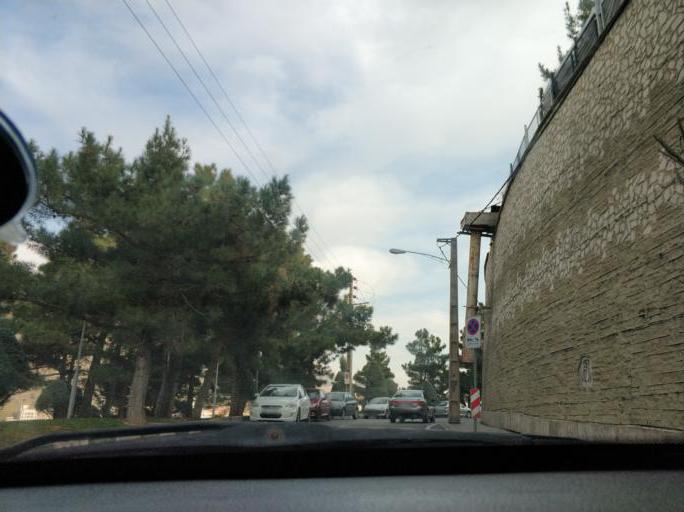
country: IR
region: Tehran
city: Tajrish
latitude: 35.8159
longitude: 51.4868
